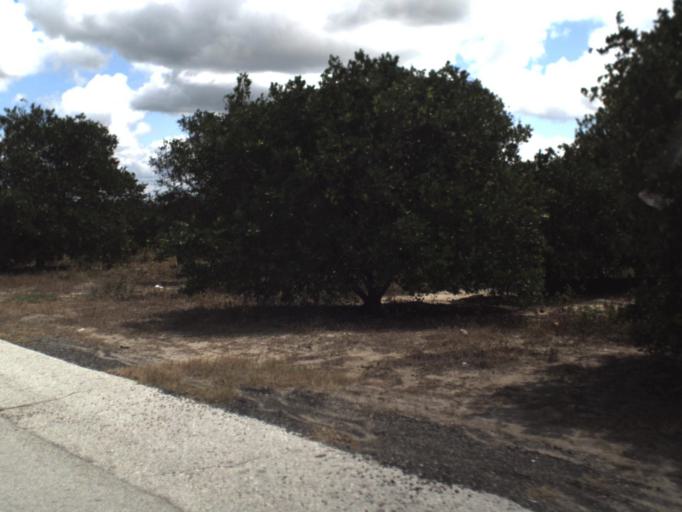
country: US
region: Florida
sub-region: Polk County
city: Fort Meade
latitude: 27.7335
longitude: -81.6930
